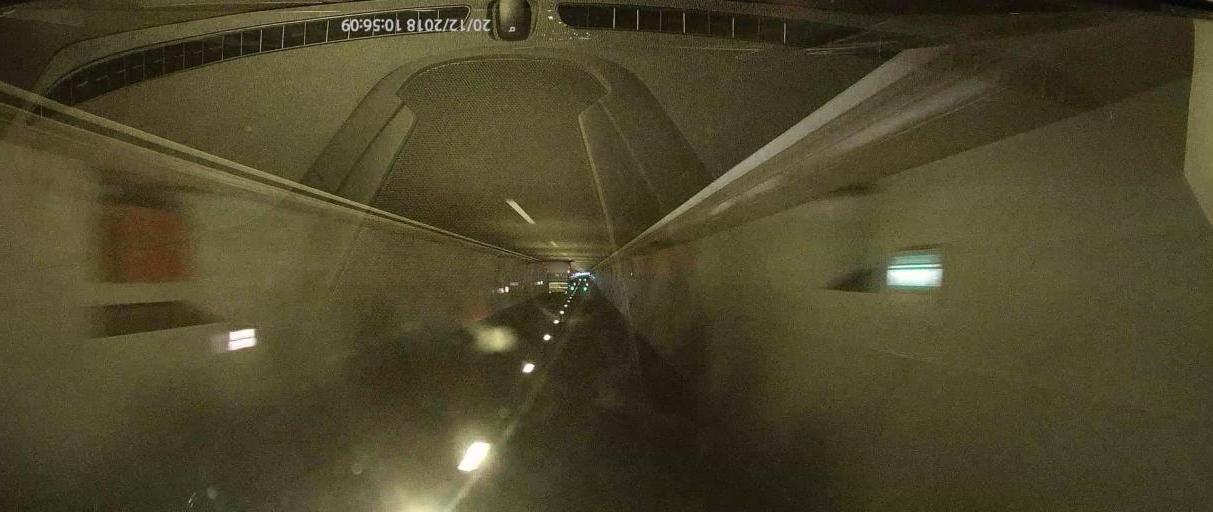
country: GR
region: Peloponnese
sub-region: Nomos Arkadias
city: Tripoli
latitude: 37.6594
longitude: 22.4724
